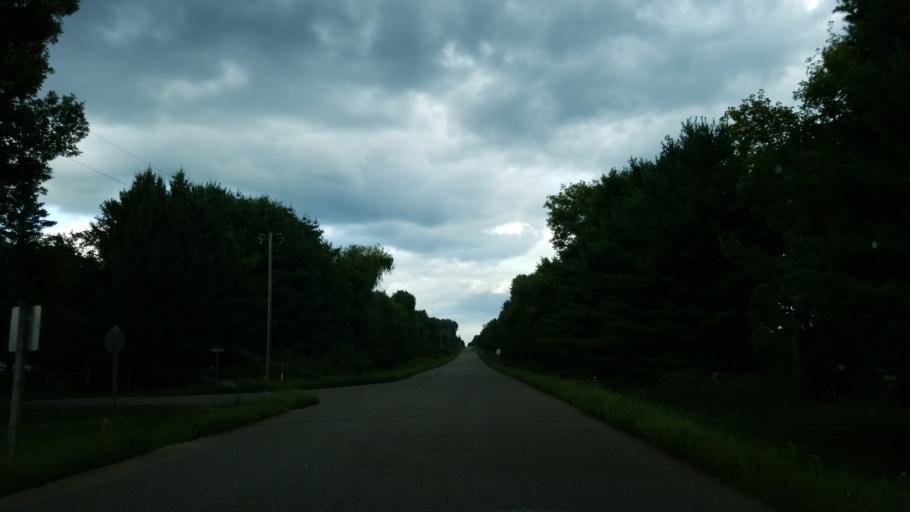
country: US
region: Minnesota
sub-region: Washington County
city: Afton
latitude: 44.8804
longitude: -92.7531
